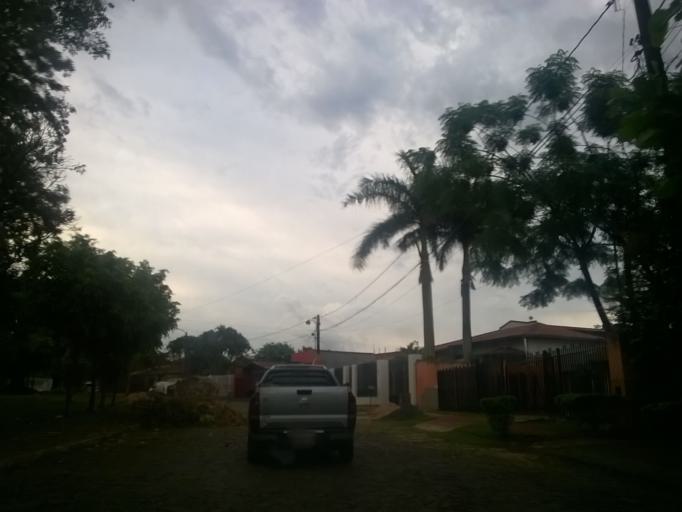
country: PY
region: Alto Parana
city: Presidente Franco
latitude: -25.5353
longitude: -54.6261
